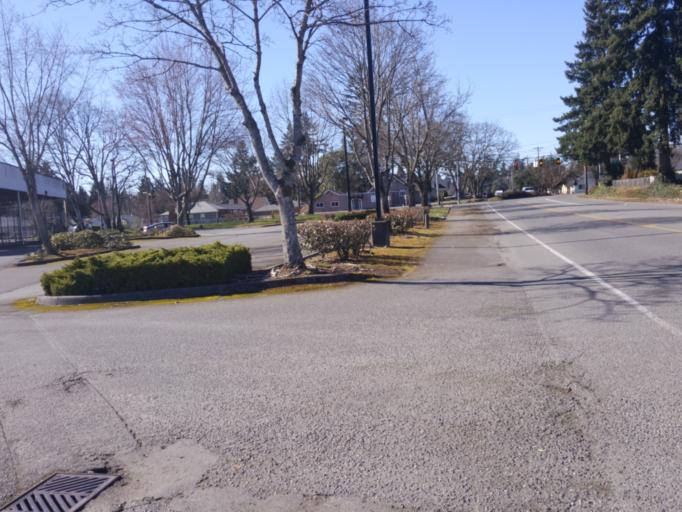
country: US
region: Washington
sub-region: Pierce County
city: Lakewood
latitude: 47.1733
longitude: -122.5202
